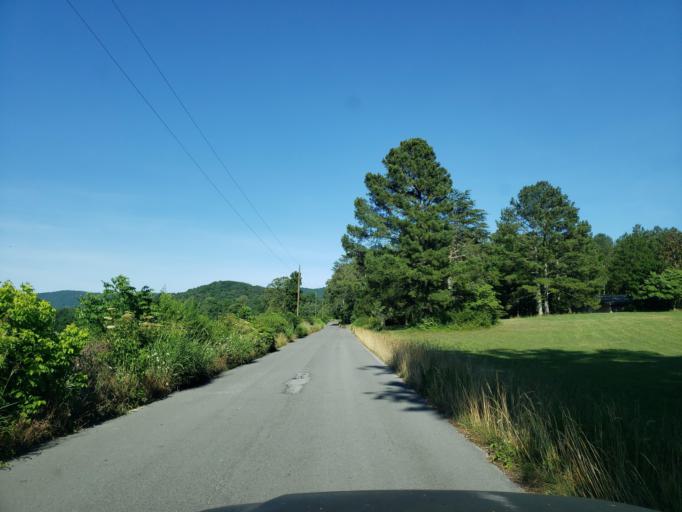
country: US
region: Georgia
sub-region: Whitfield County
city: Dalton
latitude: 34.6658
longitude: -85.1041
